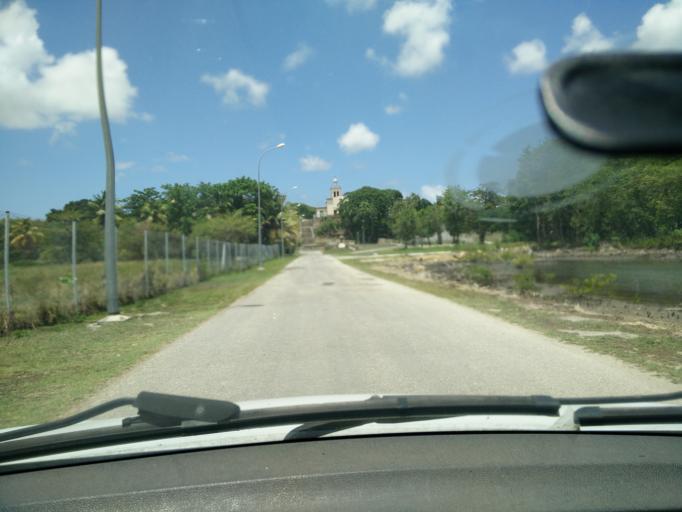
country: GP
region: Guadeloupe
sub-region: Guadeloupe
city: Petit-Canal
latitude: 16.3786
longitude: -61.4946
